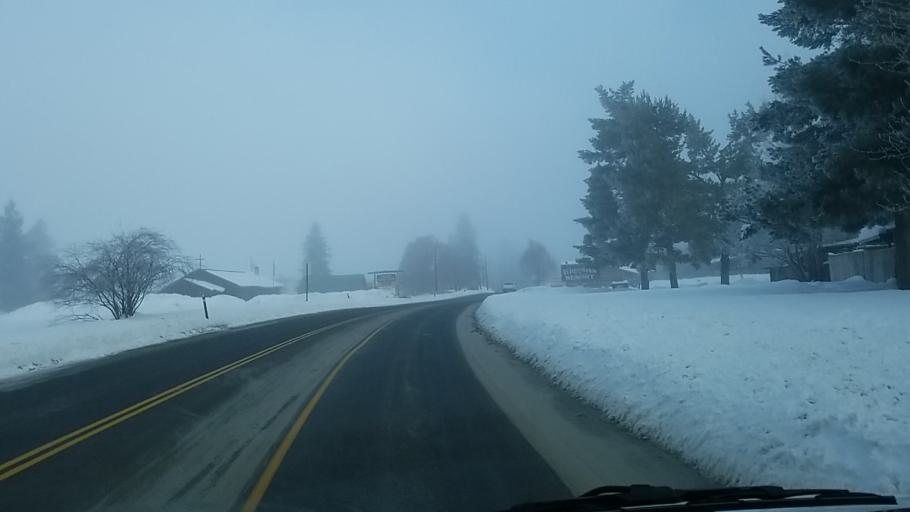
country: US
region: Washington
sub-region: Okanogan County
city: Brewster
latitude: 48.4677
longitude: -120.1761
